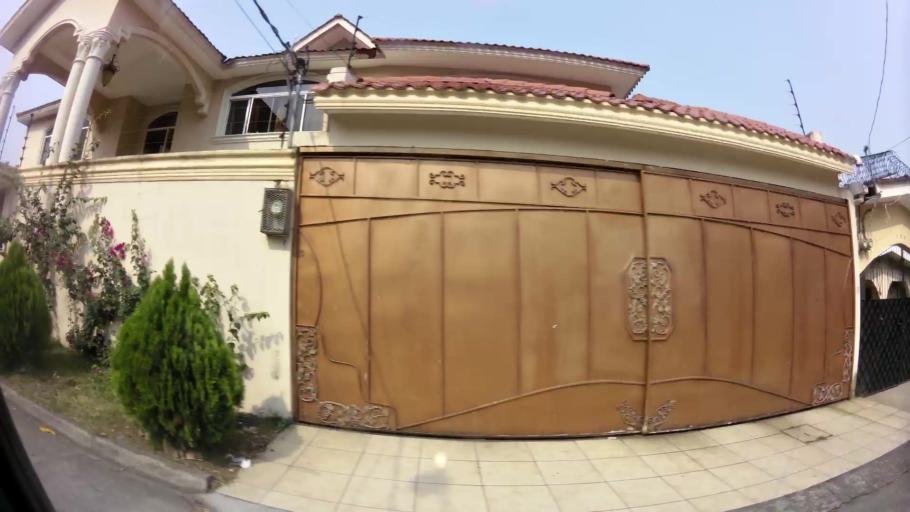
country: HN
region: Cortes
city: Armenta
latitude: 15.4950
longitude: -88.0438
